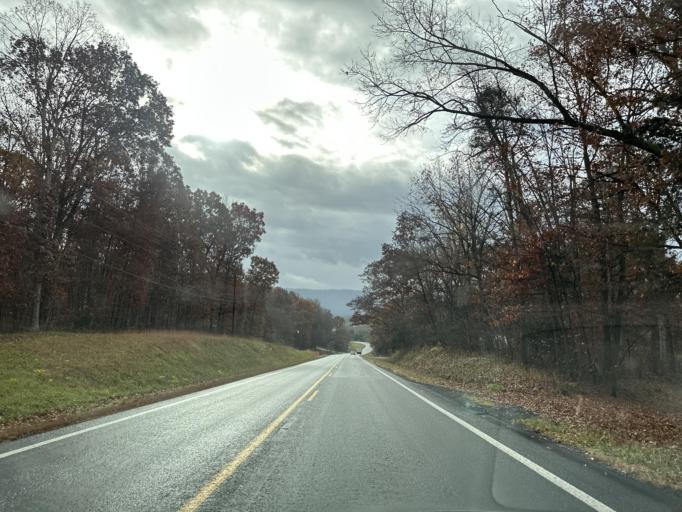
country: US
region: Virginia
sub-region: Shenandoah County
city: Strasburg
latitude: 38.9597
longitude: -78.4323
